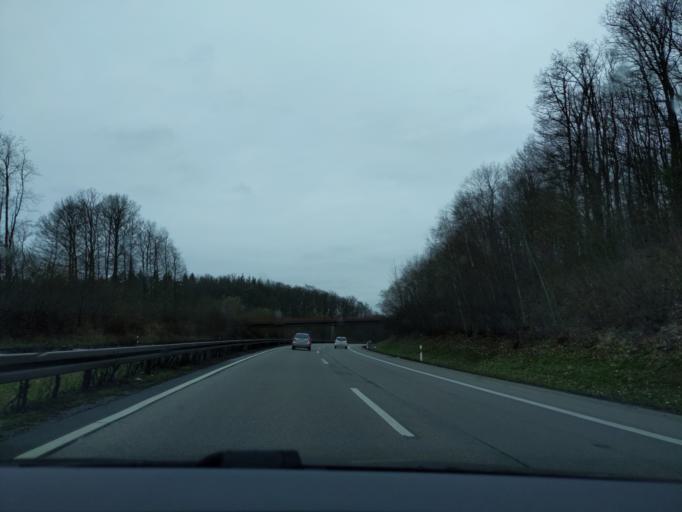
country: DE
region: Hesse
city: Staufenberg
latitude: 50.6727
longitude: 8.7200
